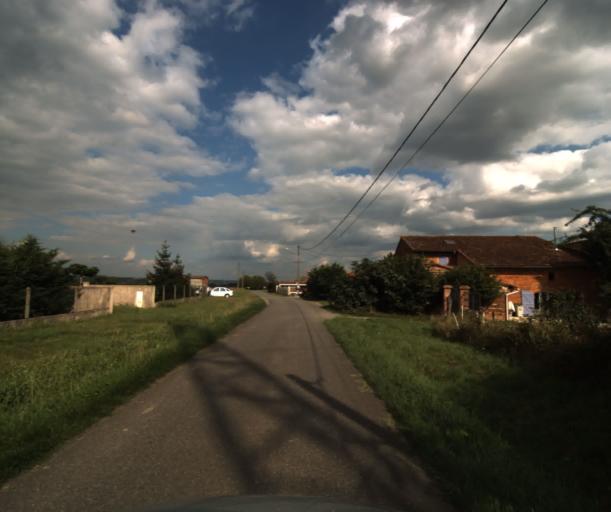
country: FR
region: Midi-Pyrenees
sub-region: Departement de la Haute-Garonne
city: Eaunes
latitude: 43.4343
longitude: 1.3717
